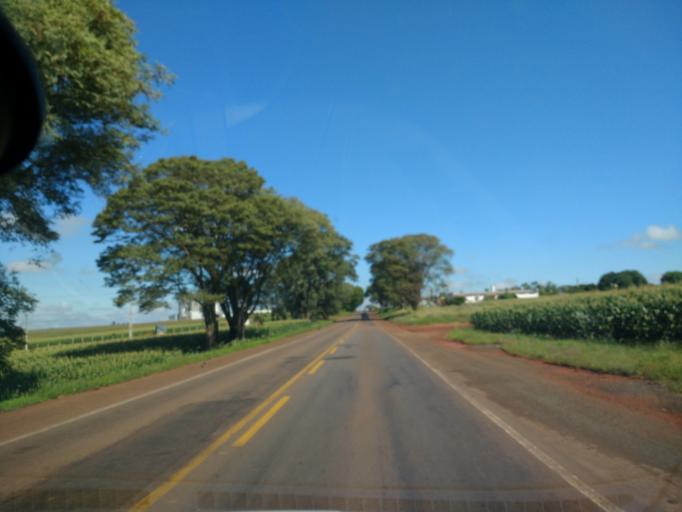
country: BR
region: Parana
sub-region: Terra Boa
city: Terra Boa
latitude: -23.6301
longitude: -52.4577
